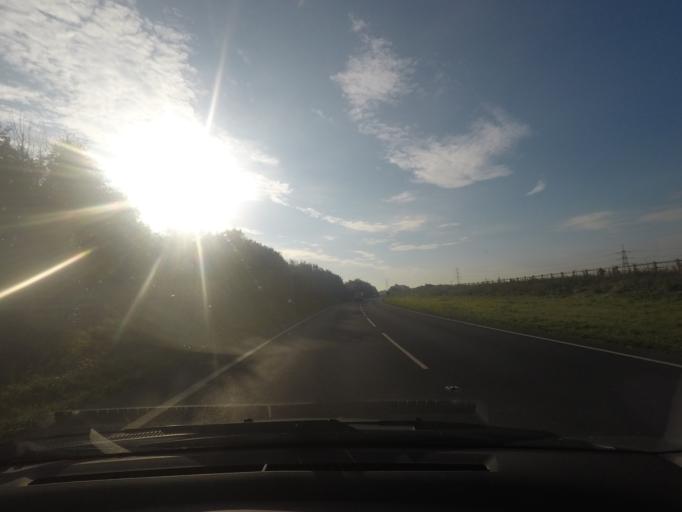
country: GB
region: England
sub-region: East Riding of Yorkshire
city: Londesborough
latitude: 53.8679
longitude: -0.6844
